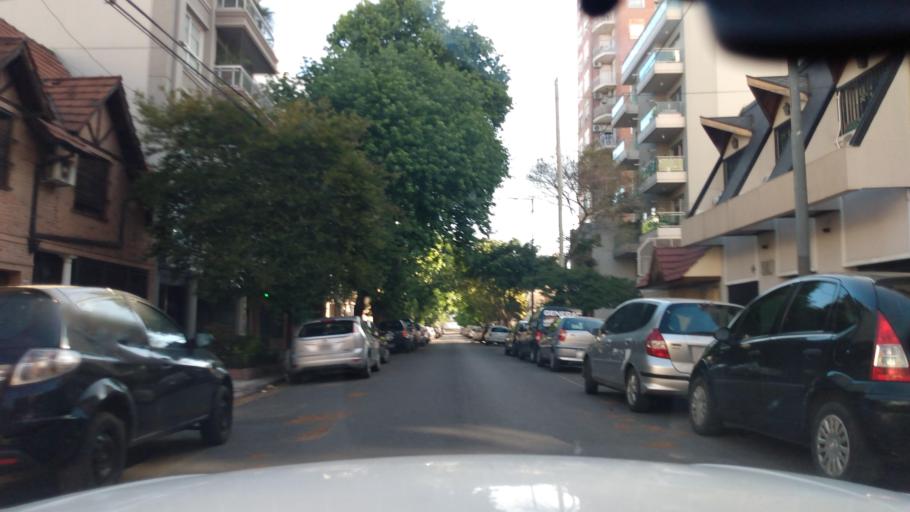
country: AR
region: Buenos Aires
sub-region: Partido de General San Martin
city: General San Martin
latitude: -34.5791
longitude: -58.4923
